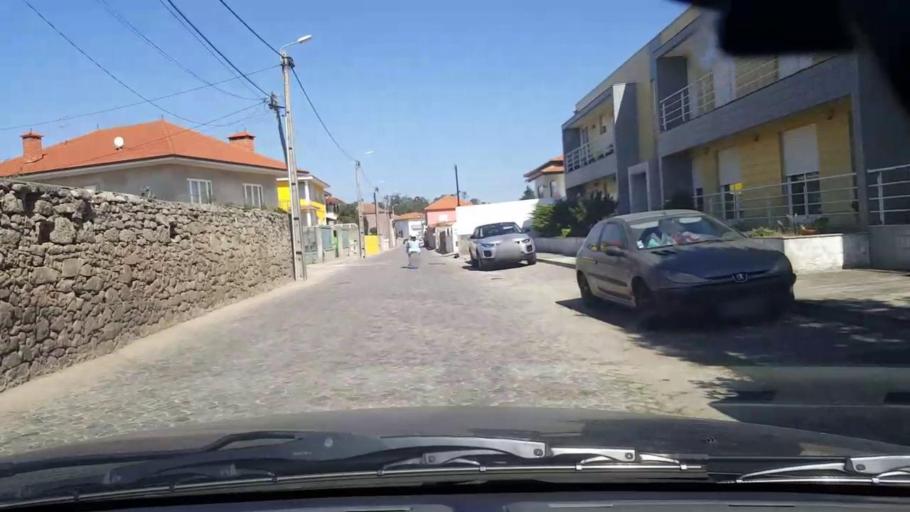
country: PT
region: Porto
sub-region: Matosinhos
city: Lavra
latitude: 41.2951
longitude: -8.7215
